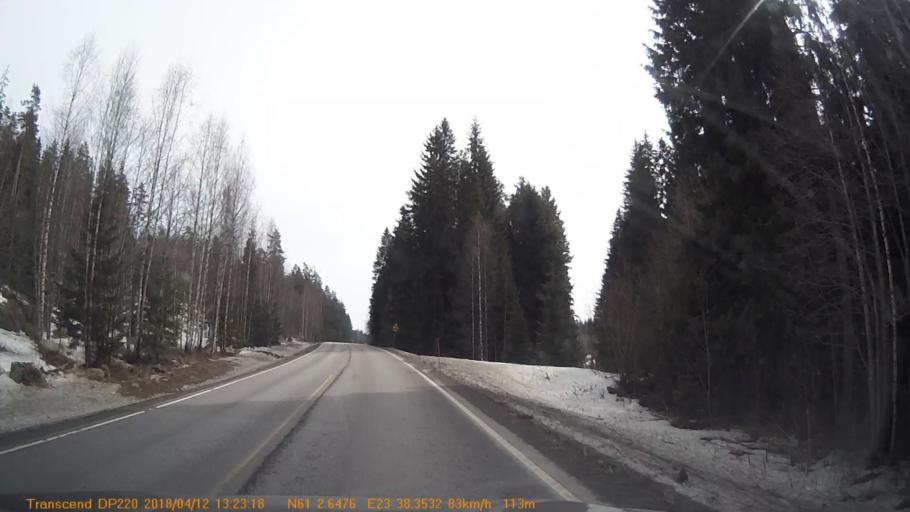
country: FI
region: Pirkanmaa
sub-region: Etelae-Pirkanmaa
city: Urjala
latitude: 61.0433
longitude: 23.6403
